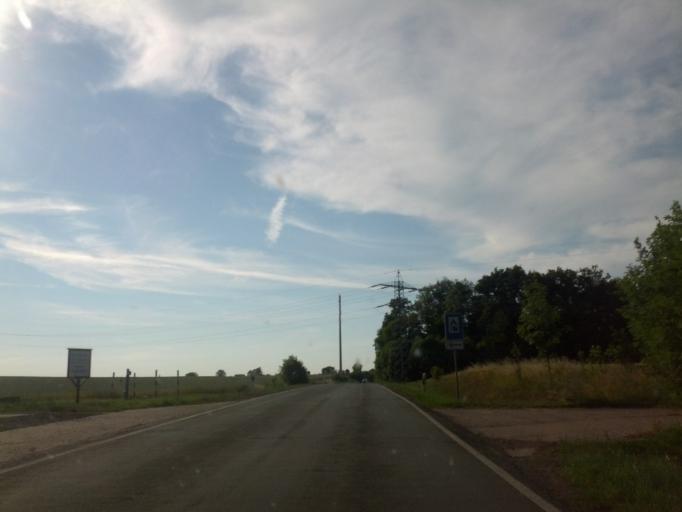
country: DE
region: Thuringia
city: Wandersleben
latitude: 50.8751
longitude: 10.8104
